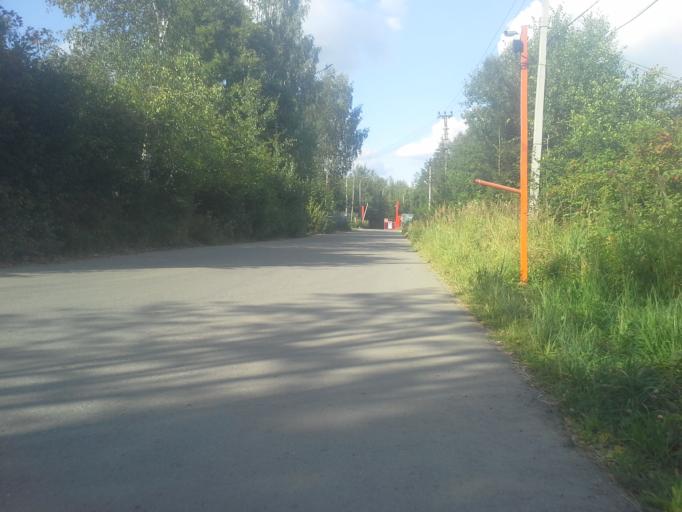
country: RU
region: Moskovskaya
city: Kievskij
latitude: 55.3531
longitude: 36.9510
